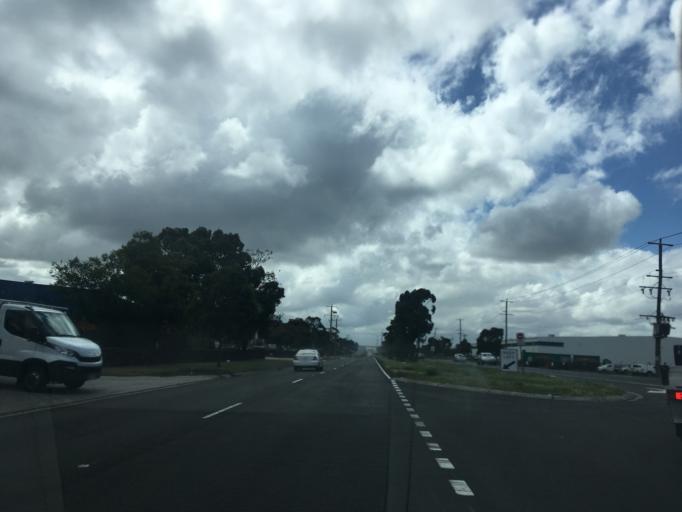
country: AU
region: Victoria
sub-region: Brimbank
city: Derrimut
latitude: -37.8173
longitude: 144.7868
